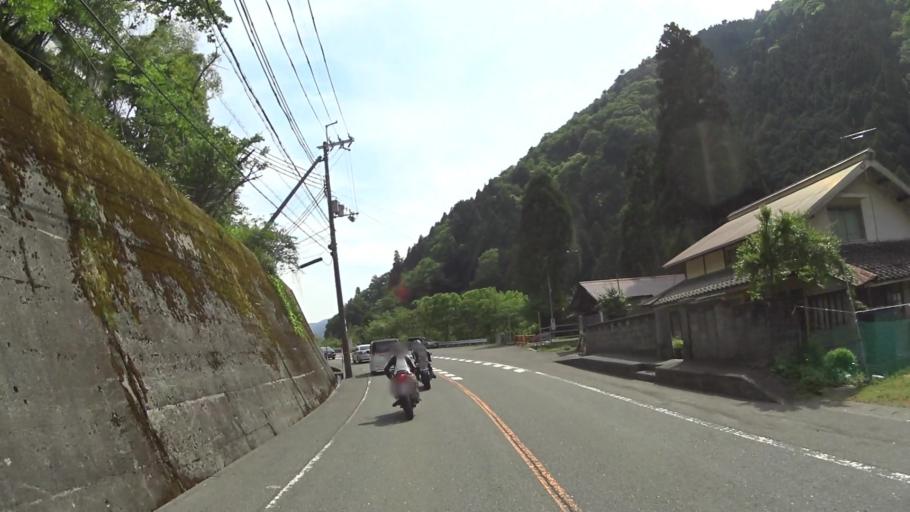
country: JP
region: Shiga Prefecture
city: Kitahama
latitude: 35.2747
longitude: 135.8776
